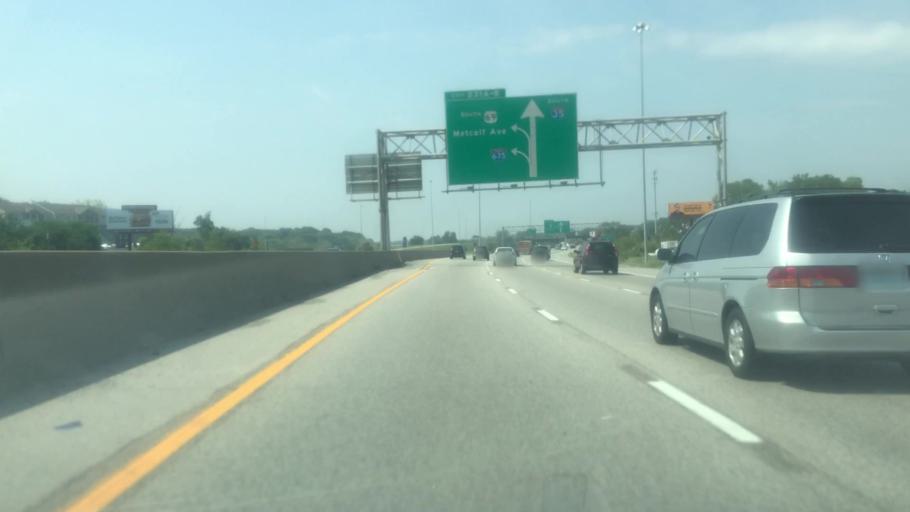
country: US
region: Kansas
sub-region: Johnson County
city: Mission
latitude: 39.0426
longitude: -94.6641
